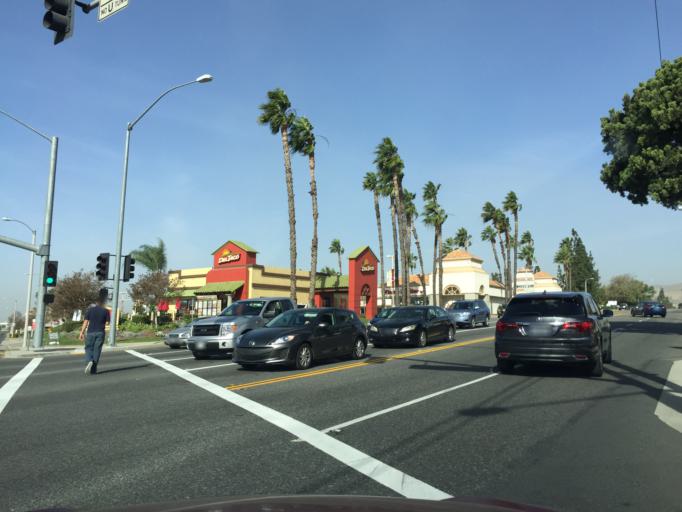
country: US
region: California
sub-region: Orange County
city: Yorba Linda
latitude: 33.9044
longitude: -117.8421
